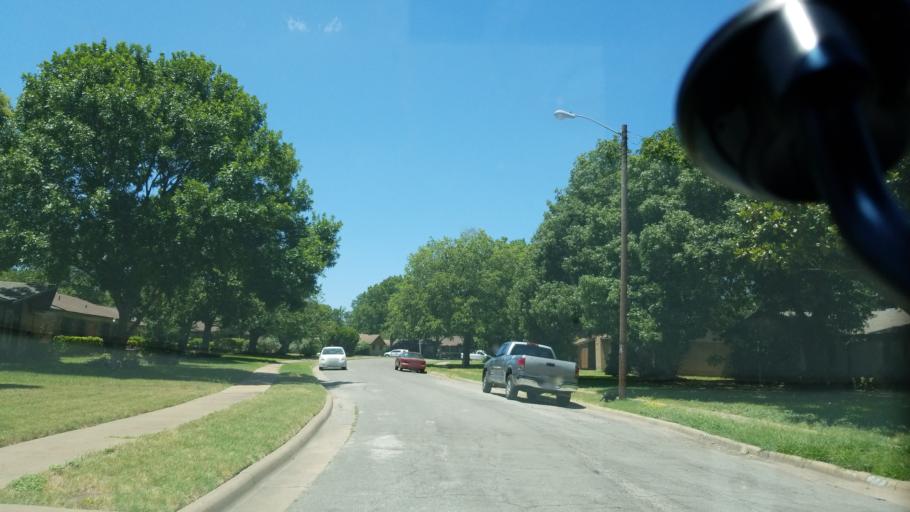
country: US
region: Texas
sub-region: Dallas County
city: Cockrell Hill
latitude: 32.6955
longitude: -96.8329
